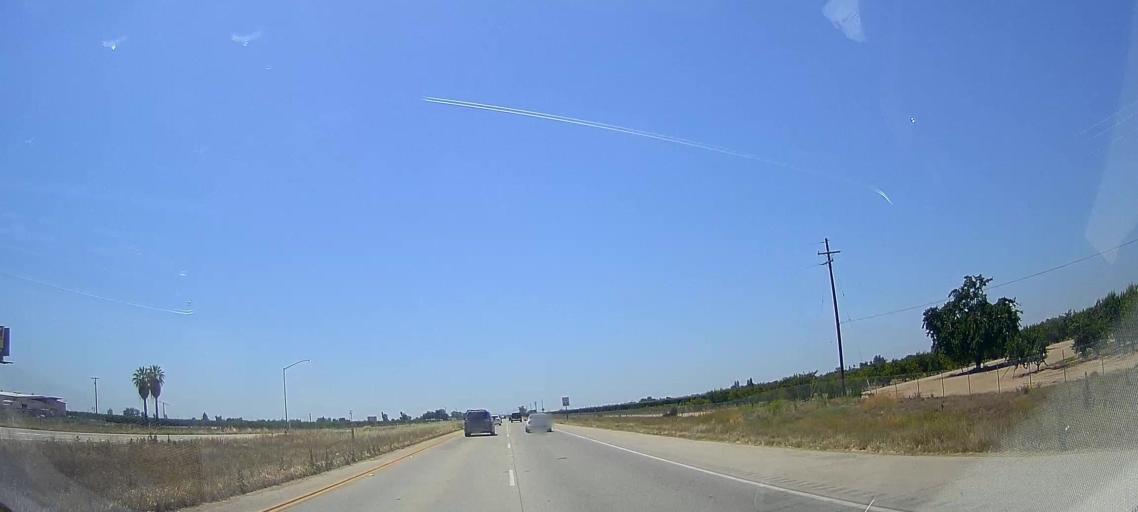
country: US
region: California
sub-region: Fresno County
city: Sanger
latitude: 36.7362
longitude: -119.5576
